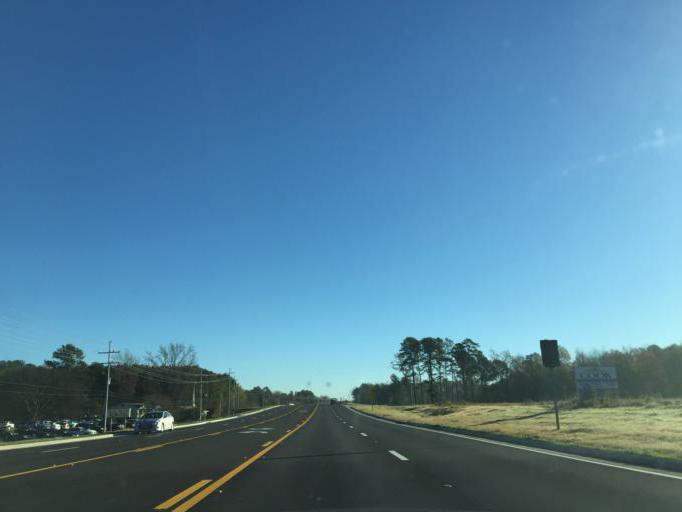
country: US
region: Mississippi
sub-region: Rankin County
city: Flowood
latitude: 32.3198
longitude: -90.1257
